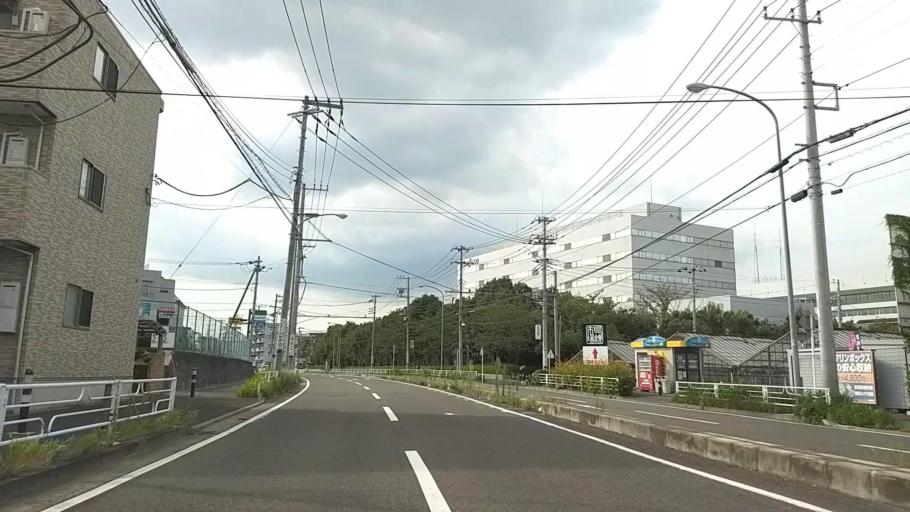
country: JP
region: Kanagawa
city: Yokohama
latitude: 35.5070
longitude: 139.5570
